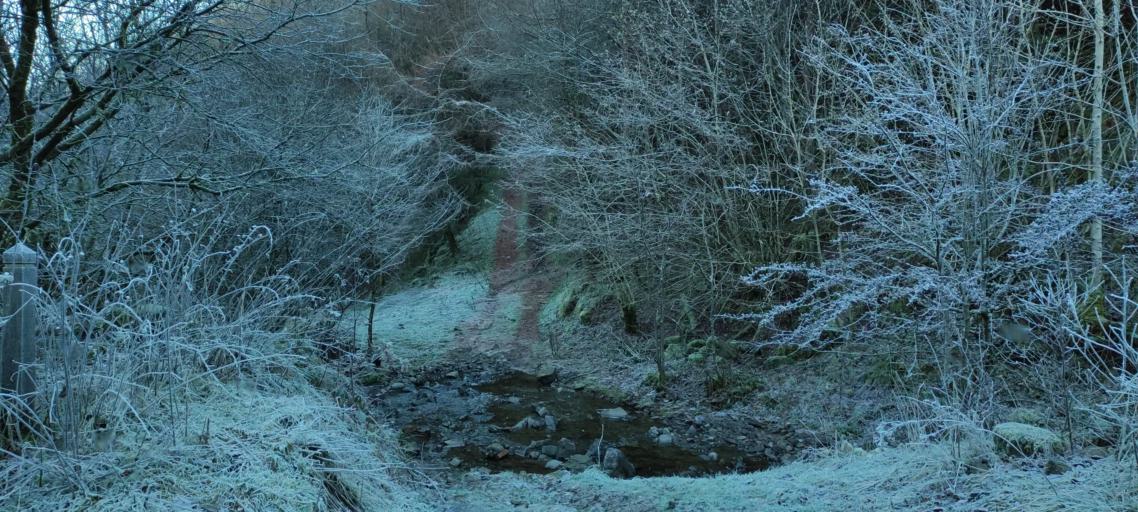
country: GB
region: Scotland
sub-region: Dumfries and Galloway
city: Langholm
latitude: 55.1663
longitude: -2.9862
